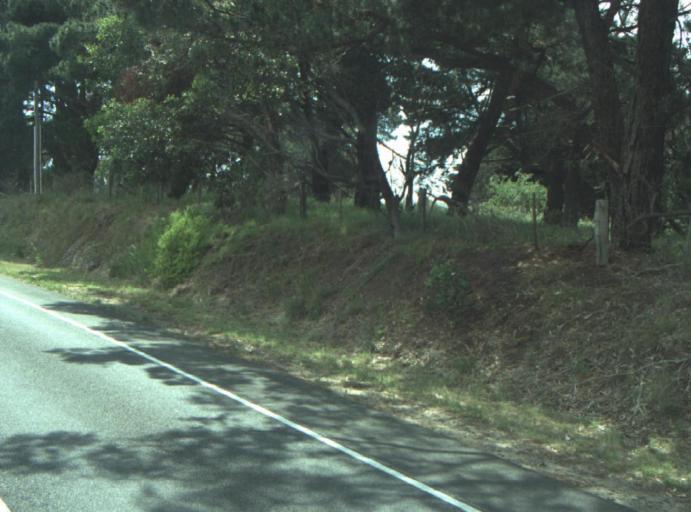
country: AU
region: Victoria
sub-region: Greater Geelong
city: Clifton Springs
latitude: -38.1531
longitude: 144.5904
